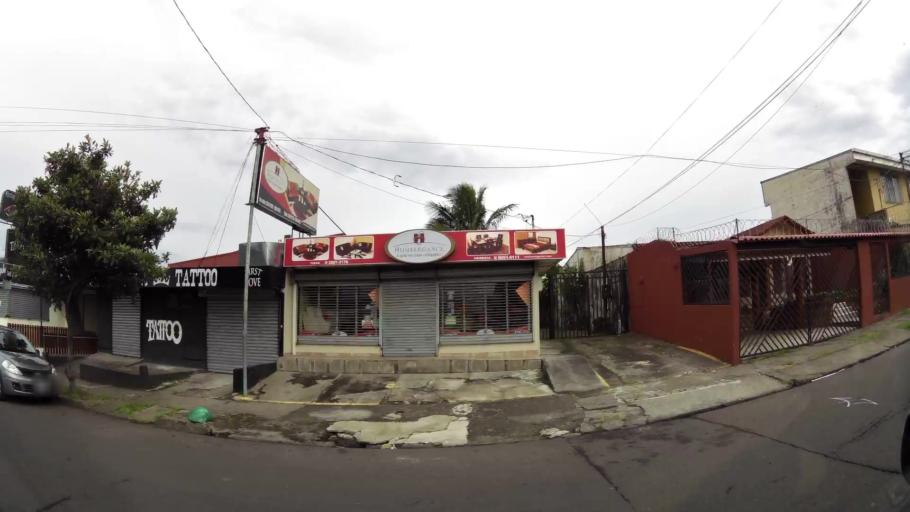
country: CR
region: San Jose
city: San Juan
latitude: 9.9625
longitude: -84.0841
